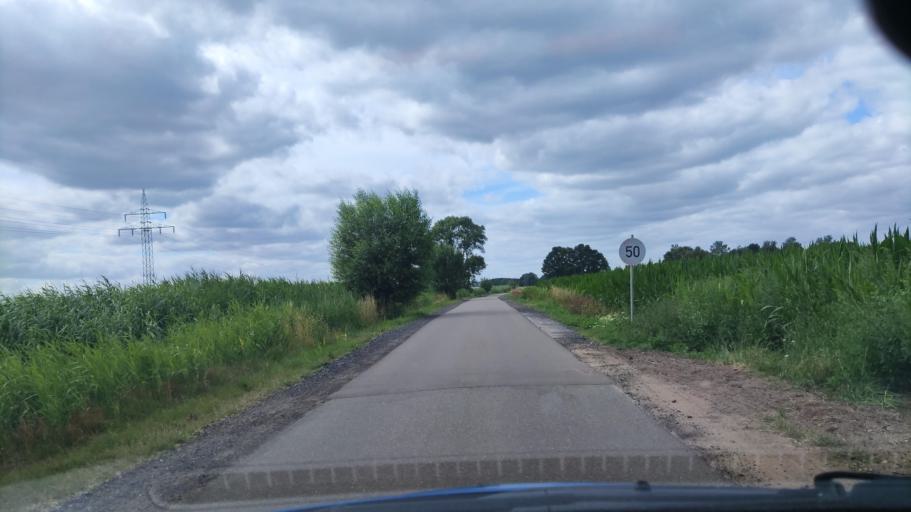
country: DE
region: Lower Saxony
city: Stelle
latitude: 53.4213
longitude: 10.0738
